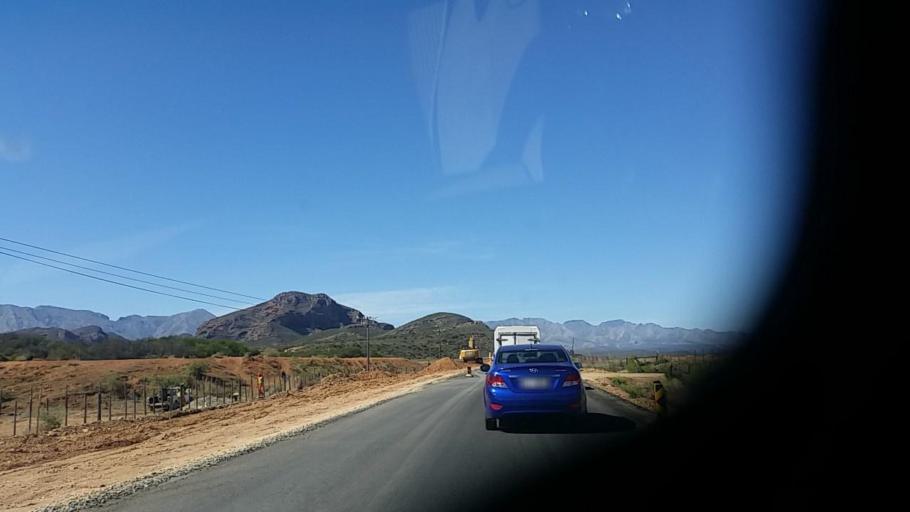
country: ZA
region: Western Cape
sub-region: Eden District Municipality
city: Oudtshoorn
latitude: -33.5550
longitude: 22.4312
